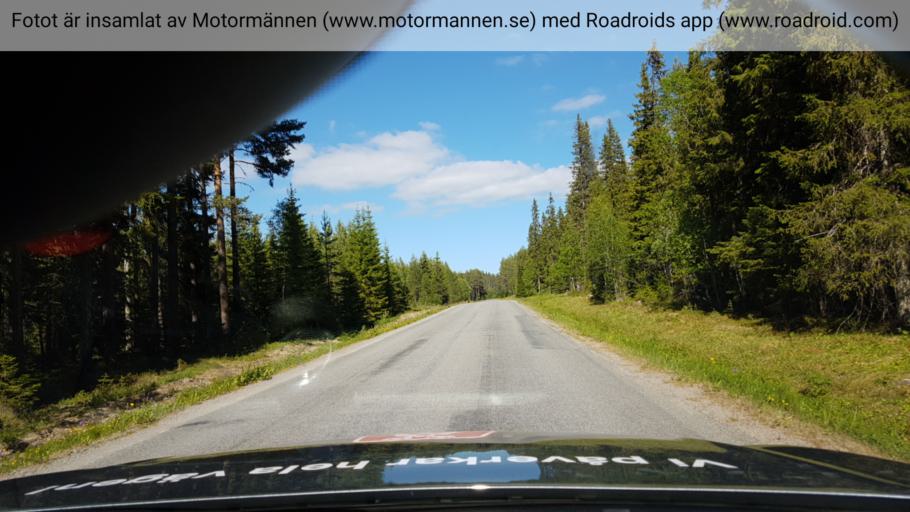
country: SE
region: Jaemtland
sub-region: OEstersunds Kommun
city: Brunflo
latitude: 63.0286
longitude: 14.8797
